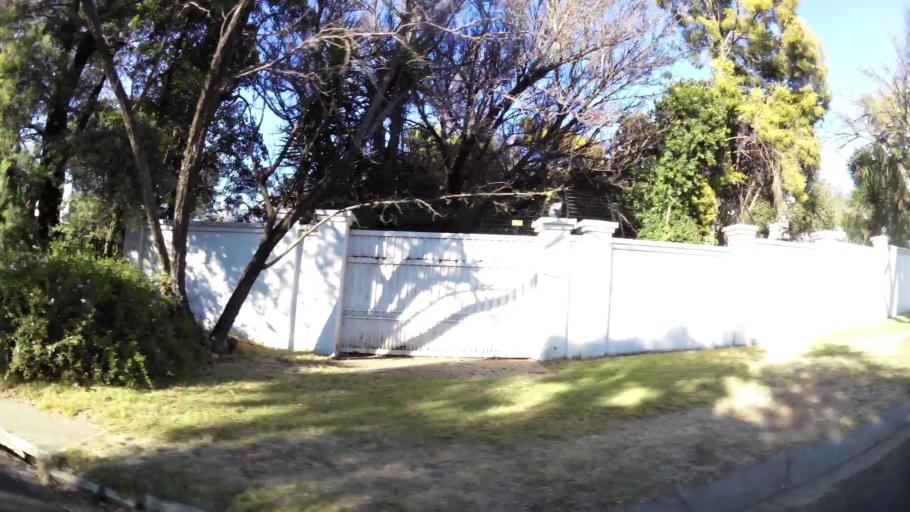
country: ZA
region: Gauteng
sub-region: City of Johannesburg Metropolitan Municipality
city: Johannesburg
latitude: -26.1499
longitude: 28.0724
